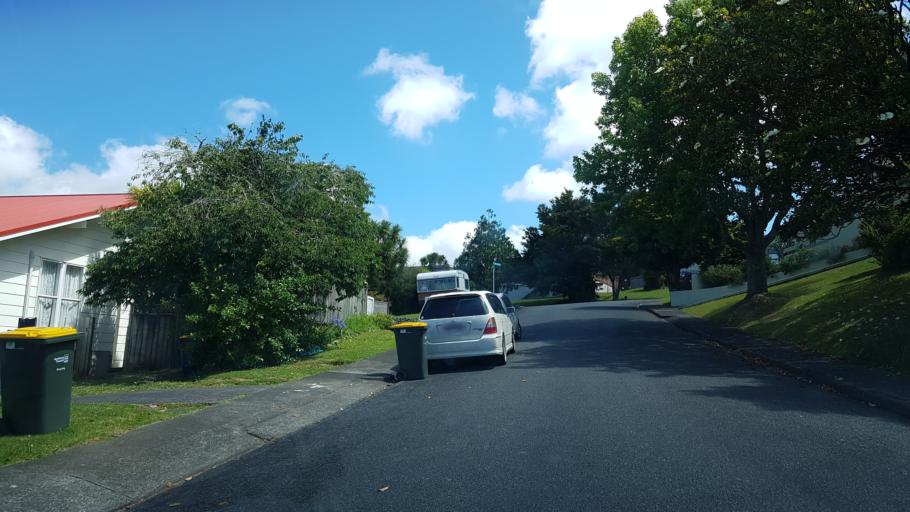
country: NZ
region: Auckland
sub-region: Auckland
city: North Shore
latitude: -36.7917
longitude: 174.7116
